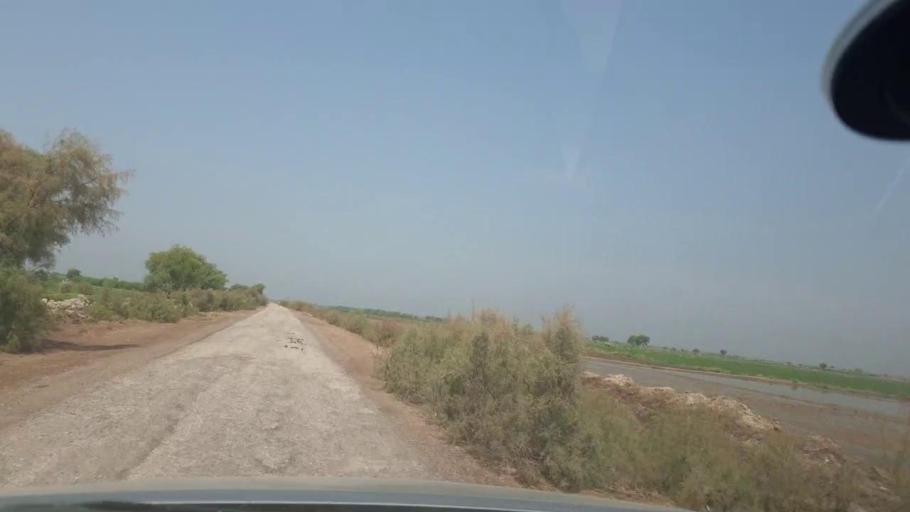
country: PK
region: Balochistan
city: Mehrabpur
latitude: 28.0602
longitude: 68.0705
